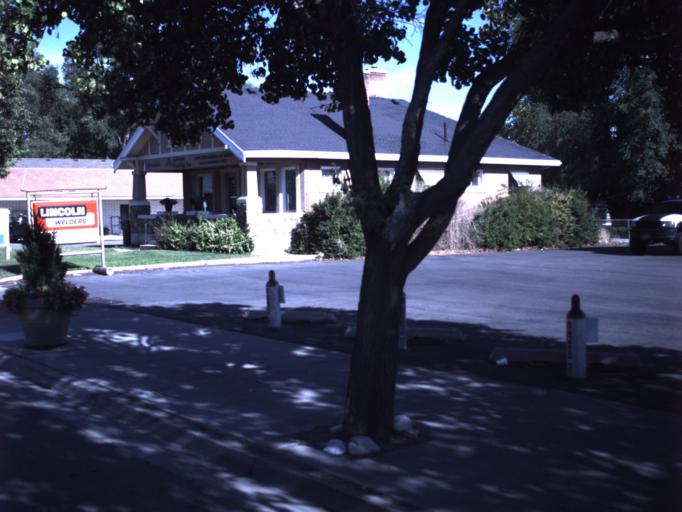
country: US
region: Utah
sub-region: Utah County
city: American Fork
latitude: 40.3767
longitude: -111.7978
